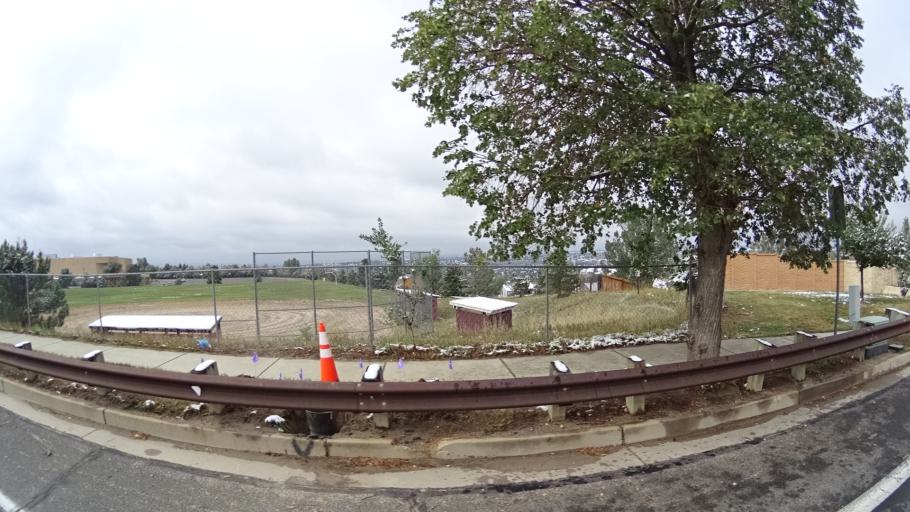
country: US
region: Colorado
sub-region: El Paso County
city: Cimarron Hills
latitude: 38.9167
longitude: -104.7602
